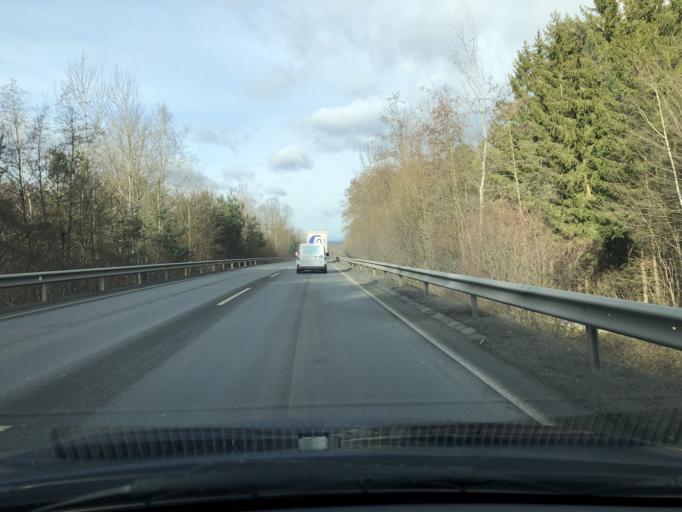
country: AT
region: Burgenland
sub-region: Politischer Bezirk Oberwart
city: Oberwart
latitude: 47.2750
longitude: 16.1999
